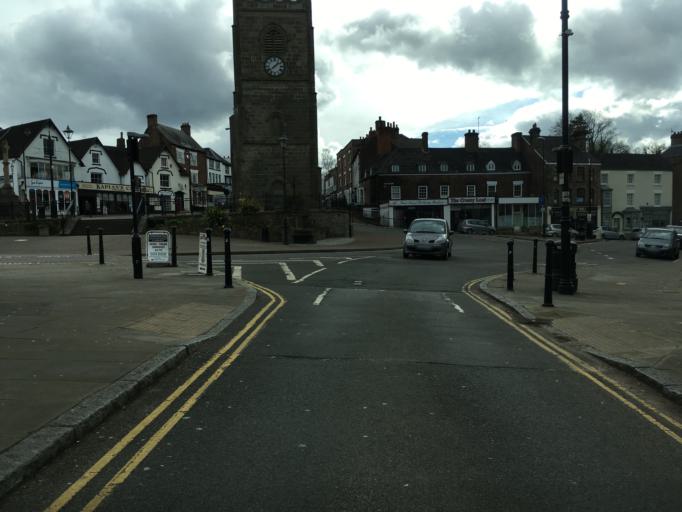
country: GB
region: England
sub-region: Gloucestershire
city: Coleford
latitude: 51.7937
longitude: -2.6177
